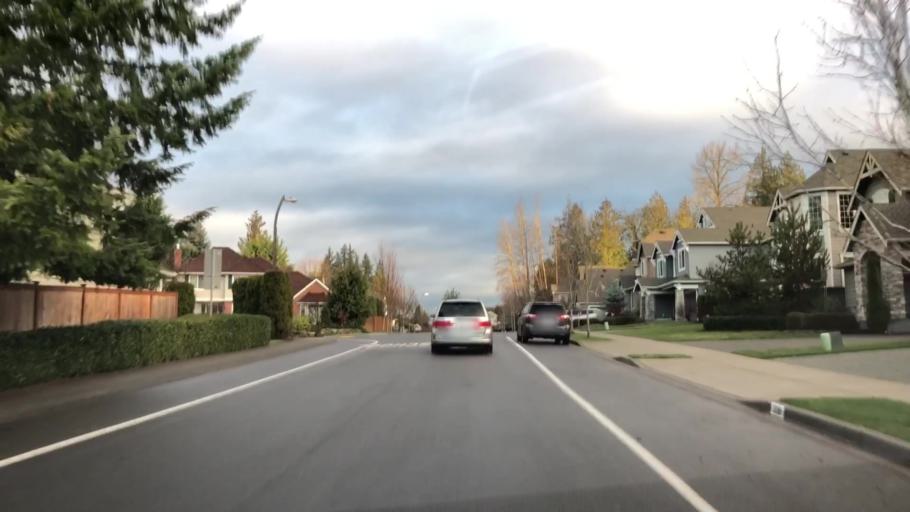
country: US
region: Washington
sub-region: King County
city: City of Sammamish
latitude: 47.6297
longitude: -122.0246
